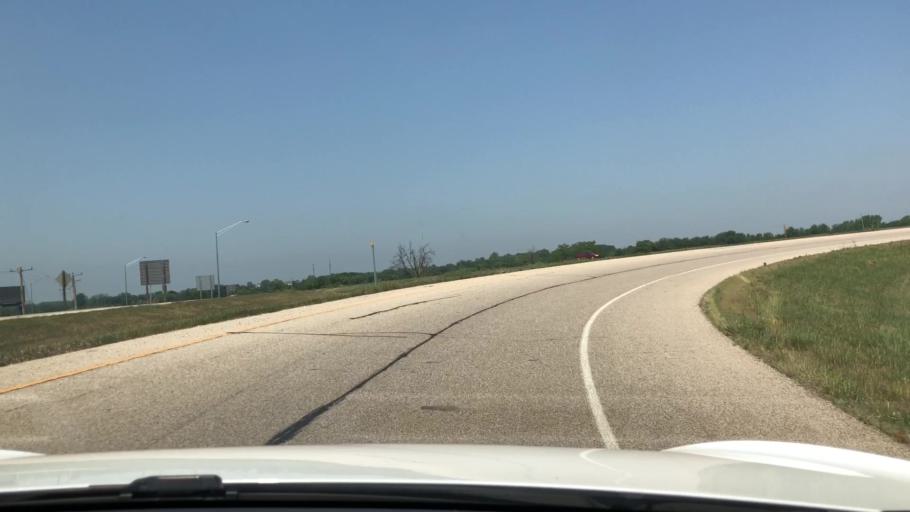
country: US
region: Illinois
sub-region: McLean County
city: Bloomington
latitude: 40.4349
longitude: -88.9921
